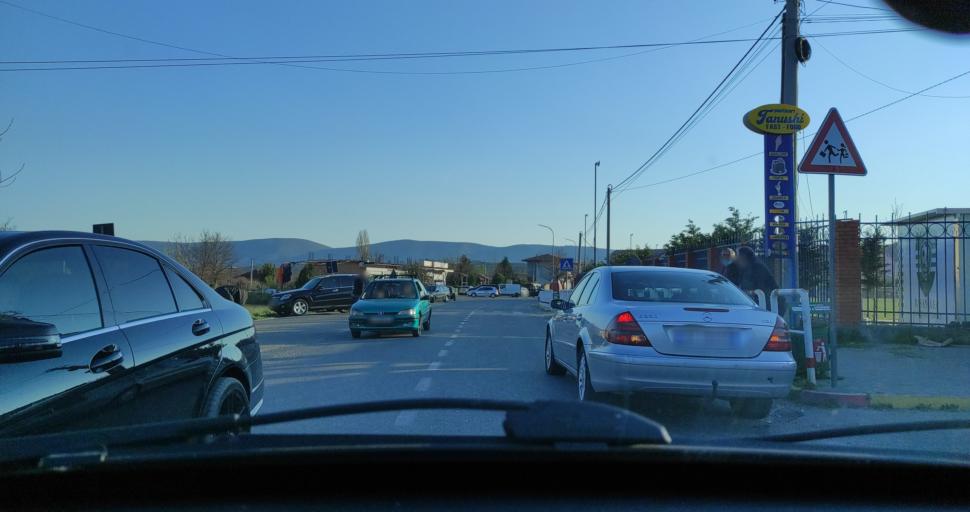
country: AL
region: Shkoder
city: Vukatane
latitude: 41.9609
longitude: 19.5363
